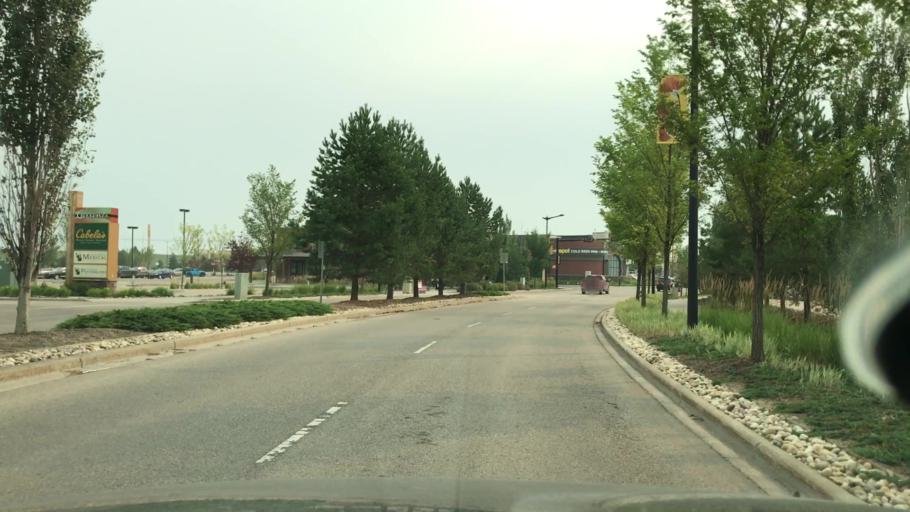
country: CA
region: Alberta
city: Devon
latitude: 53.4376
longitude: -113.6051
